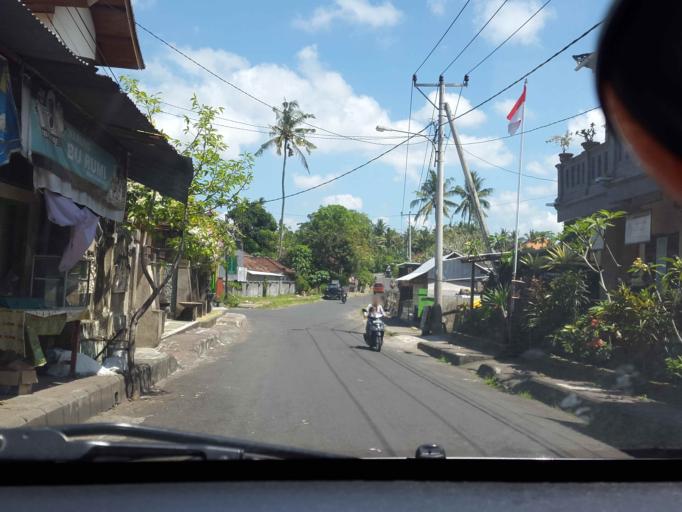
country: ID
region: Bali
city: Klungkung
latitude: -8.5245
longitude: 115.3982
